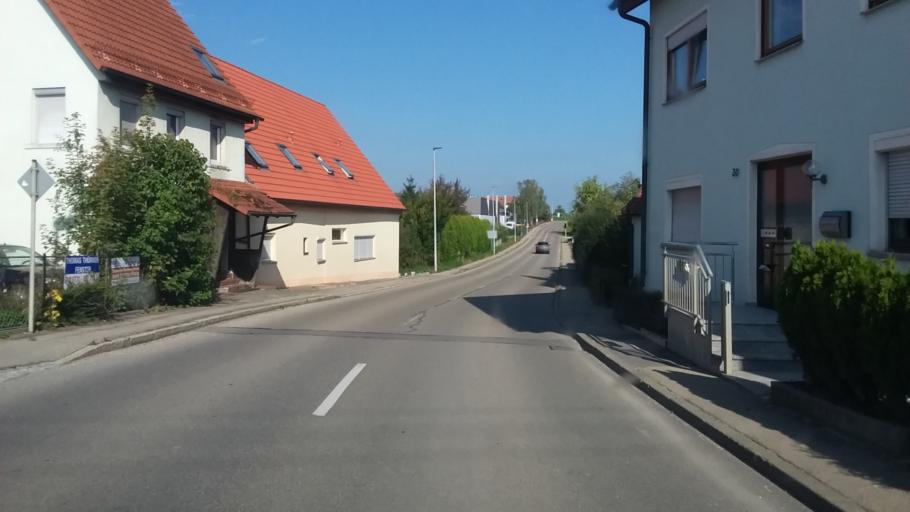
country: DE
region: Baden-Wuerttemberg
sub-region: Tuebingen Region
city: Nellingen
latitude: 48.5435
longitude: 9.7937
